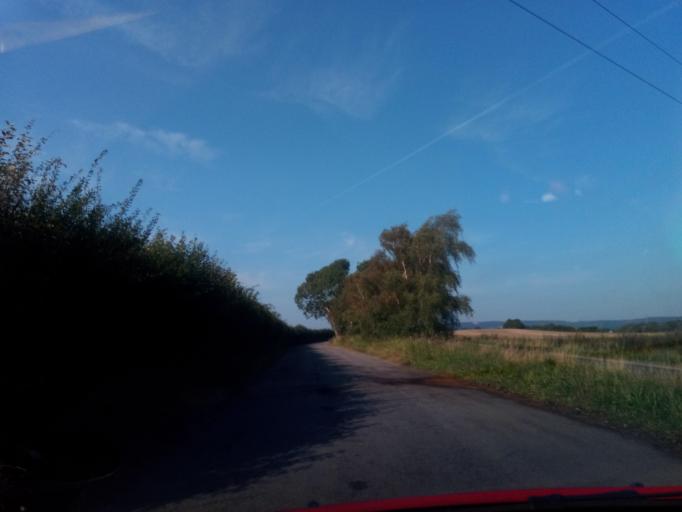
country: GB
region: England
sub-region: North Yorkshire
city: Raskelf
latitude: 54.1470
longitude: -1.2389
